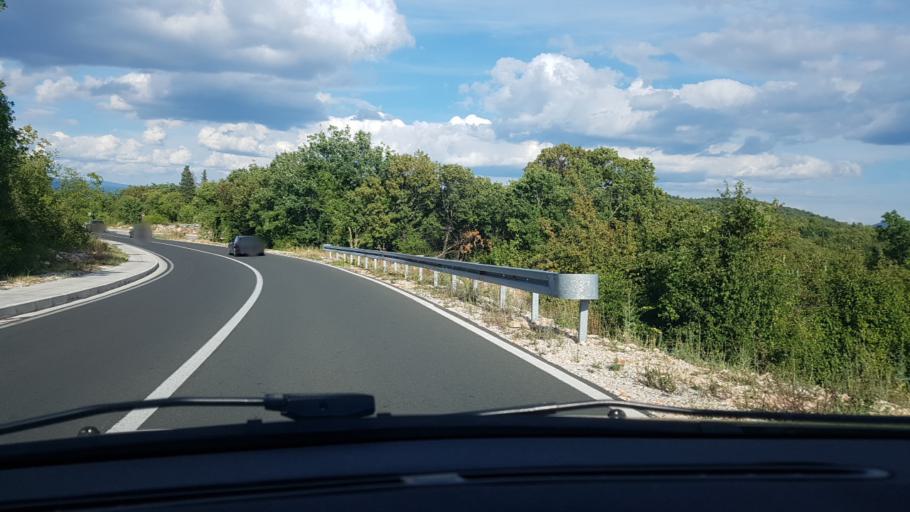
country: HR
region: Splitsko-Dalmatinska
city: Grubine
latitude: 43.4222
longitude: 17.1192
